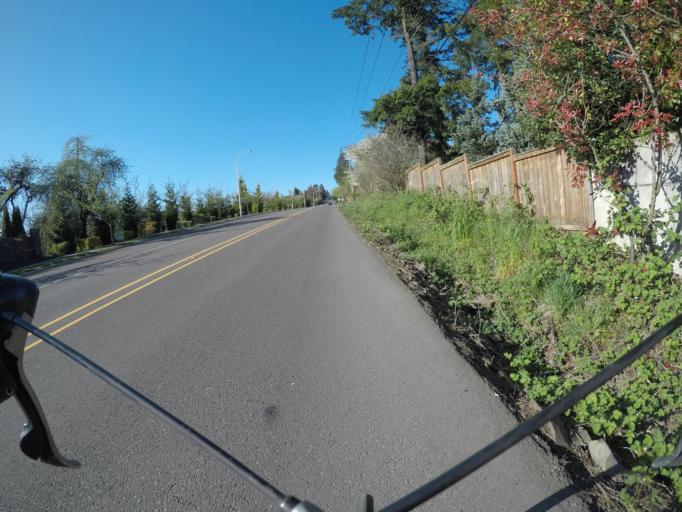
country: US
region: Oregon
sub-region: Washington County
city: King City
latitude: 45.4099
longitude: -122.8313
